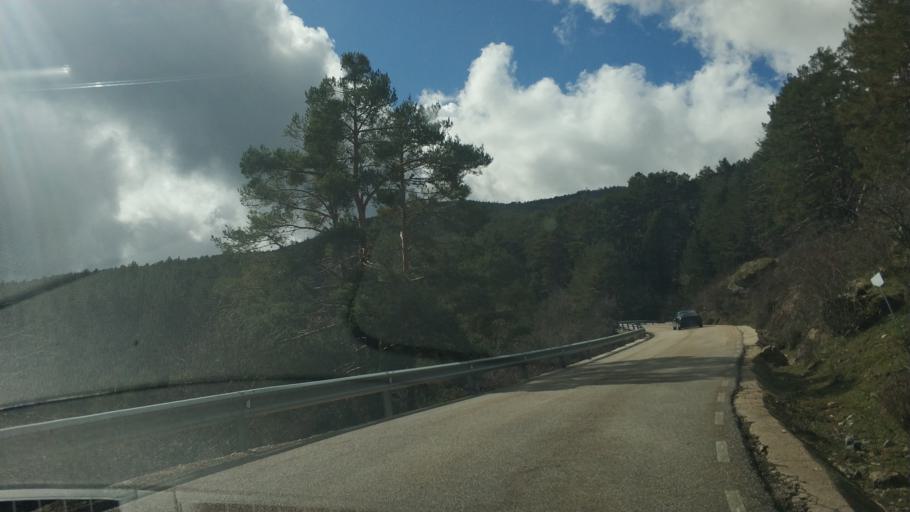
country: ES
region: Castille and Leon
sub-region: Provincia de Burgos
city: Neila
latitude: 42.0541
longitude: -3.0100
